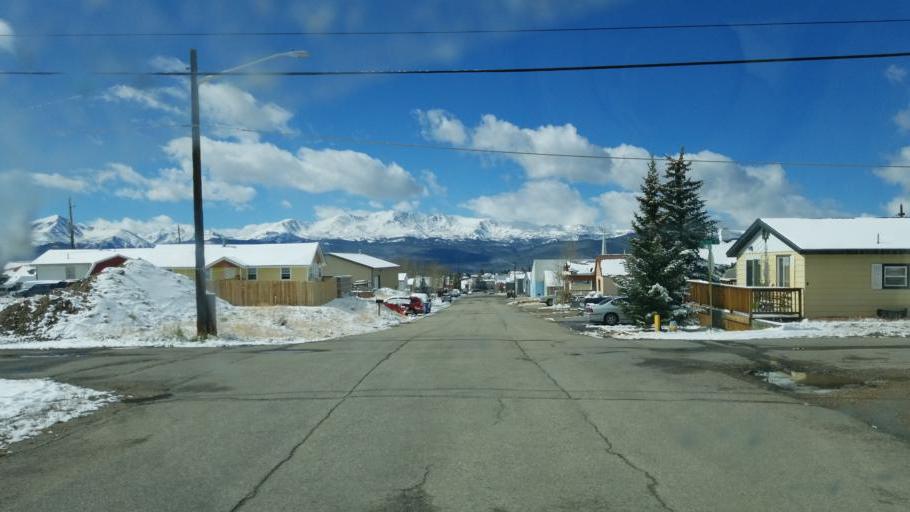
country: US
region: Colorado
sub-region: Lake County
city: Leadville
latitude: 39.2504
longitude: -106.2850
